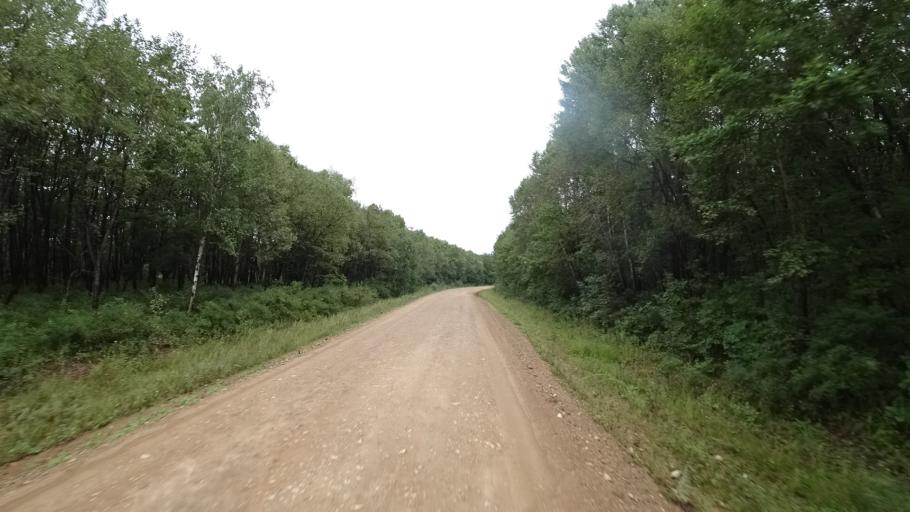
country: RU
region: Primorskiy
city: Ivanovka
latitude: 44.0513
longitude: 132.5495
